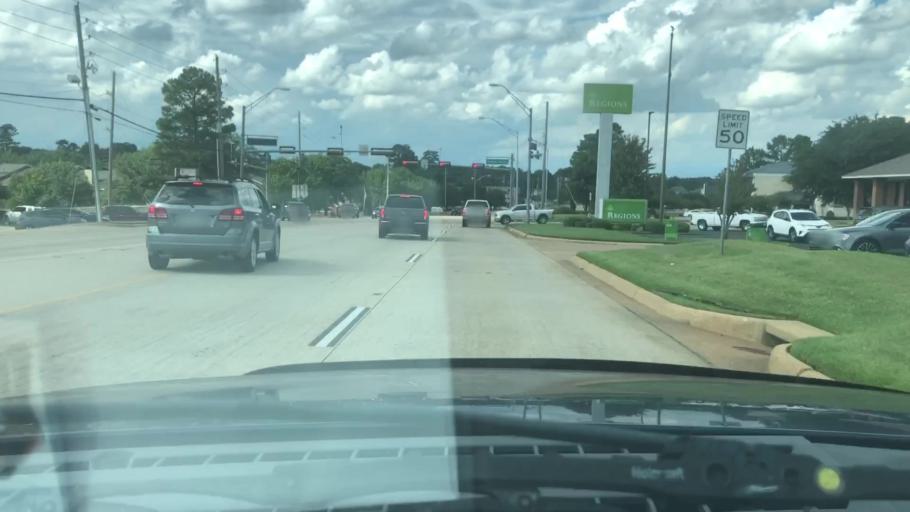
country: US
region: Arkansas
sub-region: Miller County
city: Texarkana
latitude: 33.4682
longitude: -94.0678
